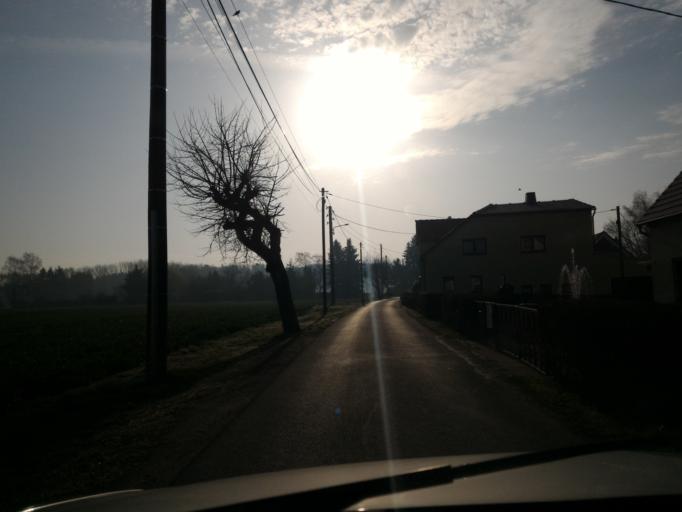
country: DE
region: Saxony
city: Leutersdorf
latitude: 50.9510
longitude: 14.6701
